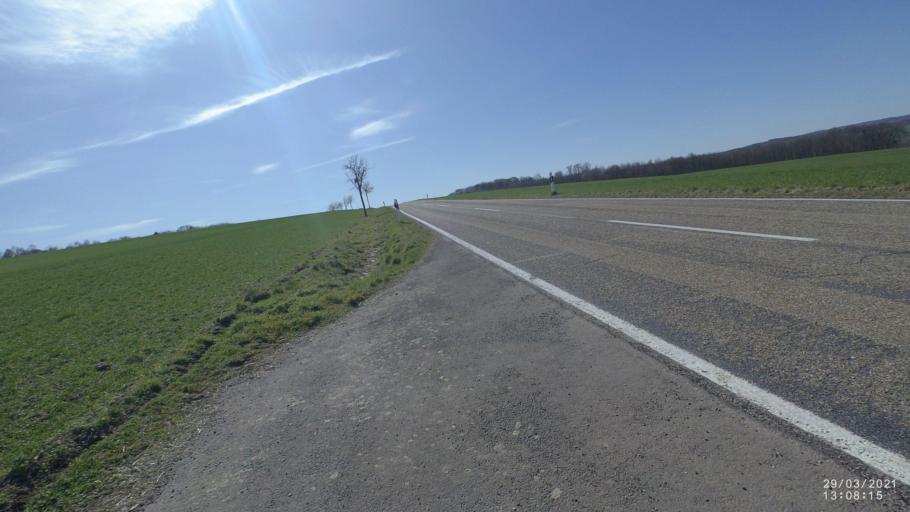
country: DE
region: Rheinland-Pfalz
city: Nickenich
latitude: 50.4425
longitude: 7.3341
